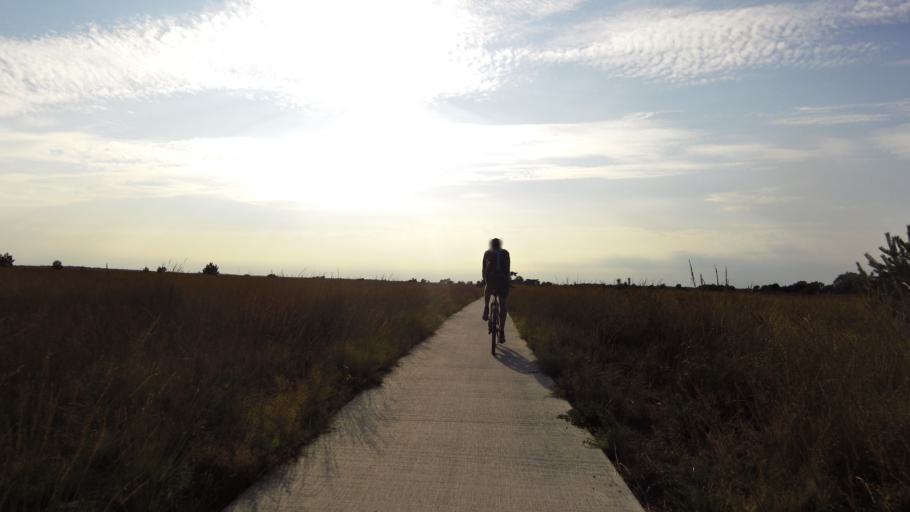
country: NL
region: Gelderland
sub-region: Gemeente Rozendaal
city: Rozendaal
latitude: 52.0399
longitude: 5.9816
